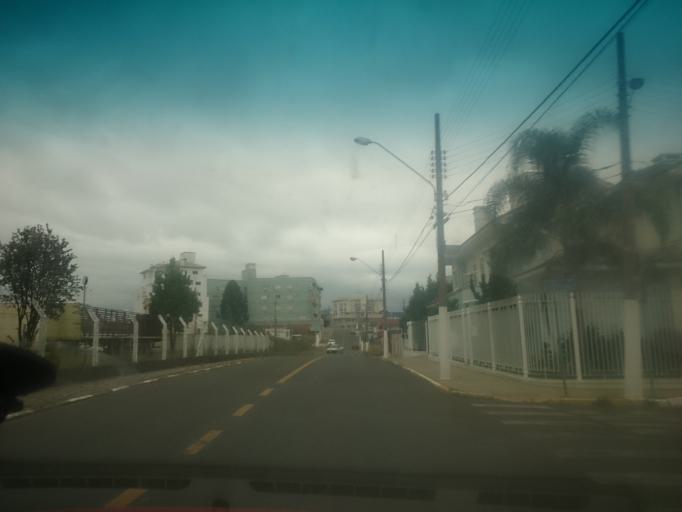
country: BR
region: Santa Catarina
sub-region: Lages
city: Lages
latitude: -27.8153
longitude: -50.3106
